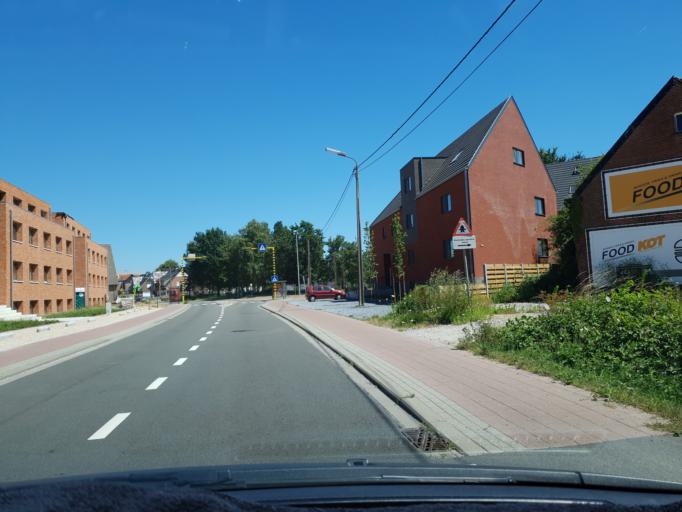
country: BE
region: Flanders
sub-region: Provincie Antwerpen
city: Geel
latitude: 51.1641
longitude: 4.9604
